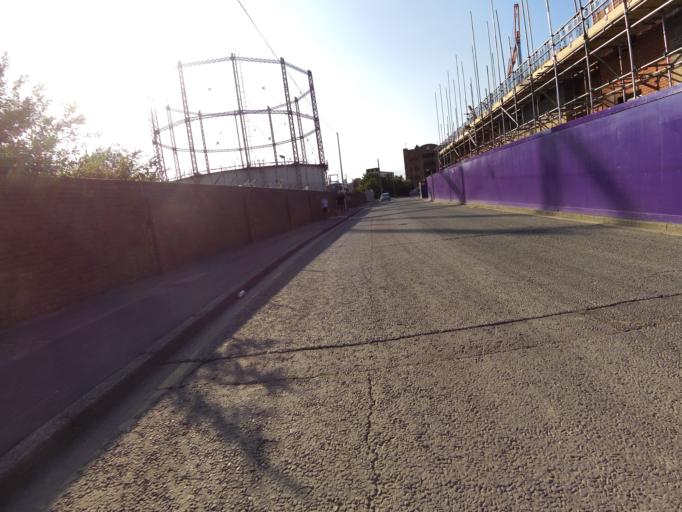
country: GB
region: England
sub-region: Essex
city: Chelmsford
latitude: 51.7315
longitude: 0.4803
